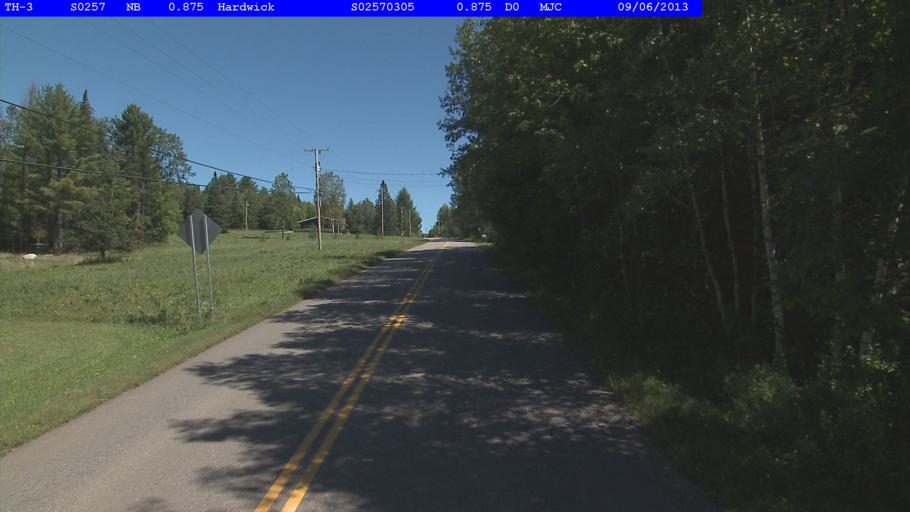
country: US
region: Vermont
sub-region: Caledonia County
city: Hardwick
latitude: 44.5068
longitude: -72.3511
